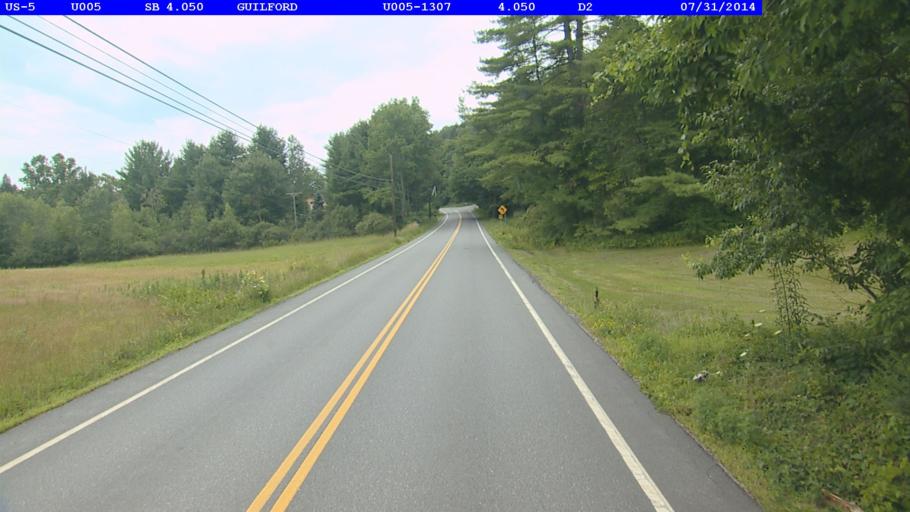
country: US
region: Vermont
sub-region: Windham County
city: Brattleboro
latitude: 42.7867
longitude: -72.5683
